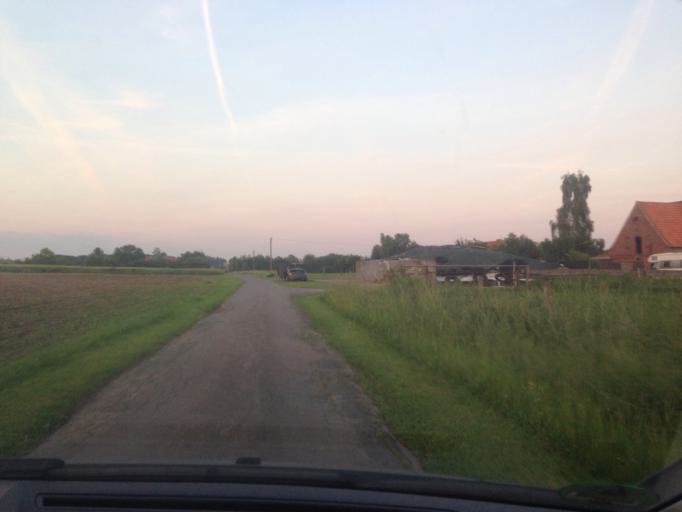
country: DE
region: North Rhine-Westphalia
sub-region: Regierungsbezirk Munster
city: Greven
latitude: 52.0224
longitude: 7.5500
